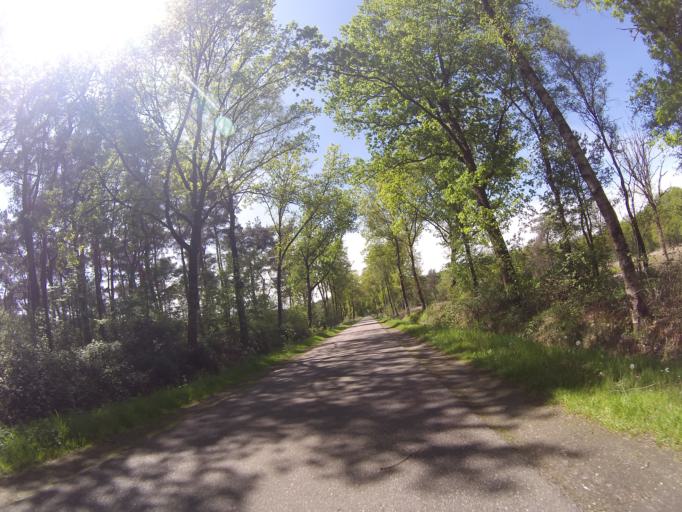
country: NL
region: Gelderland
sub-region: Gemeente Barneveld
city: Terschuur
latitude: 52.1810
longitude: 5.5513
